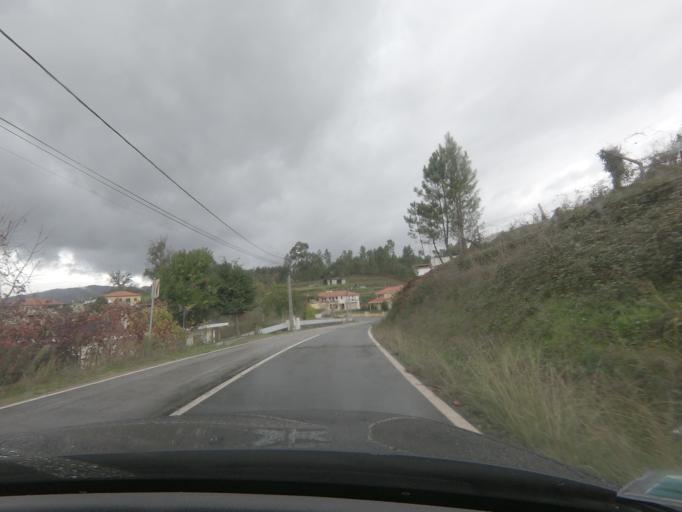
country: PT
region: Vila Real
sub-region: Mondim de Basto
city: Mondim de Basto
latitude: 41.4132
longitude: -7.9757
